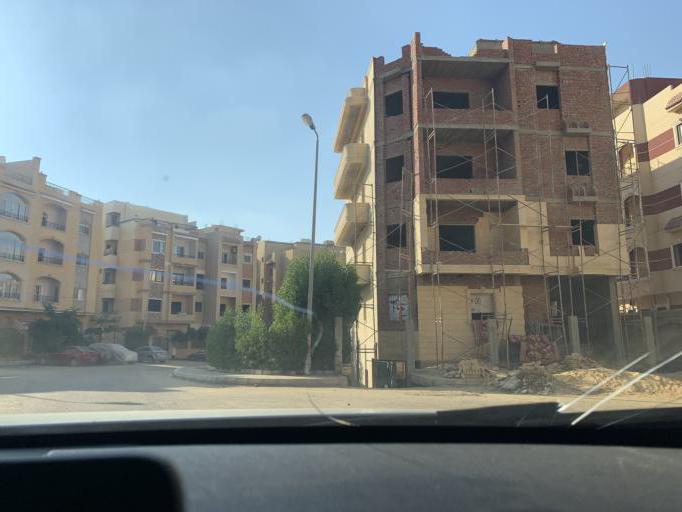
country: EG
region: Muhafazat al Qalyubiyah
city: Al Khankah
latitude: 30.0005
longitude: 31.4820
